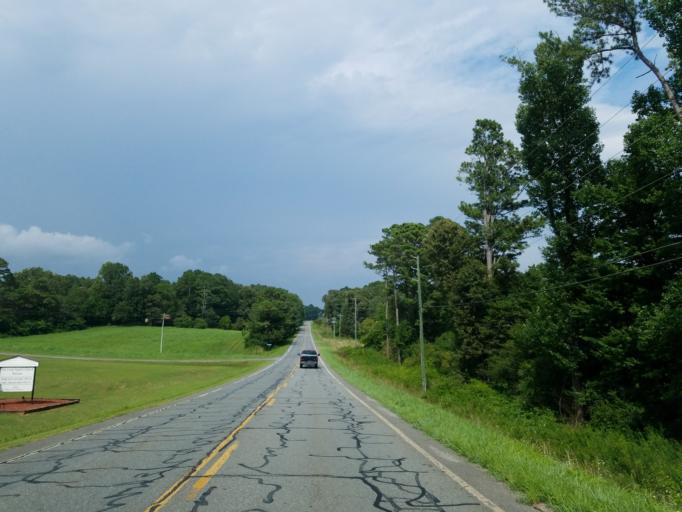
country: US
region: Georgia
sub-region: Gilmer County
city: Ellijay
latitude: 34.6407
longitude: -84.5620
